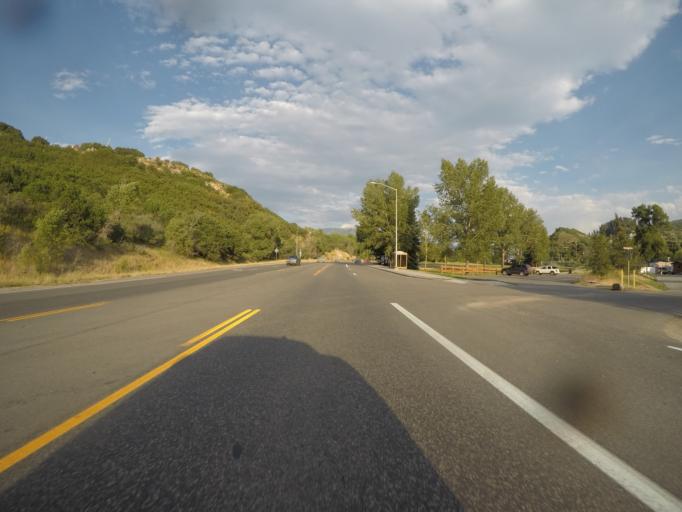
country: US
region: Colorado
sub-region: Routt County
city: Steamboat Springs
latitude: 40.4917
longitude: -106.8436
